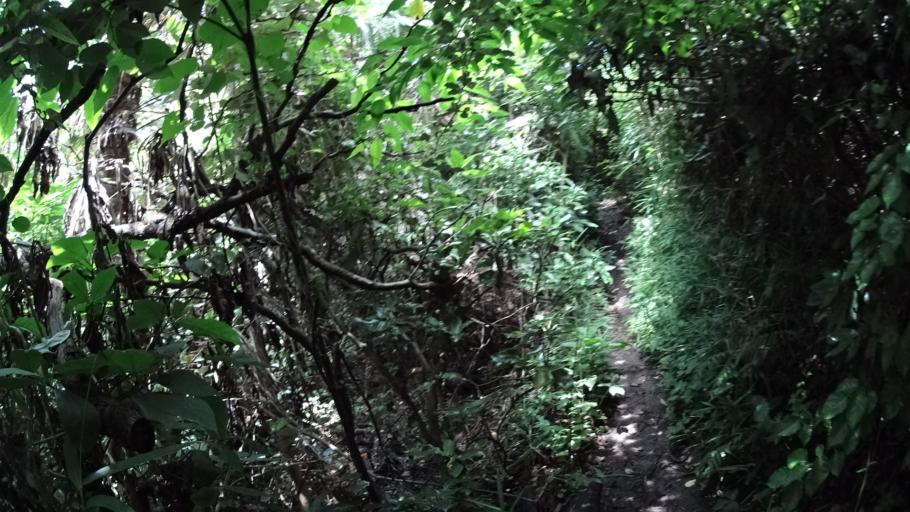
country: JP
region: Kanagawa
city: Yokosuka
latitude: 35.2120
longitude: 139.6707
